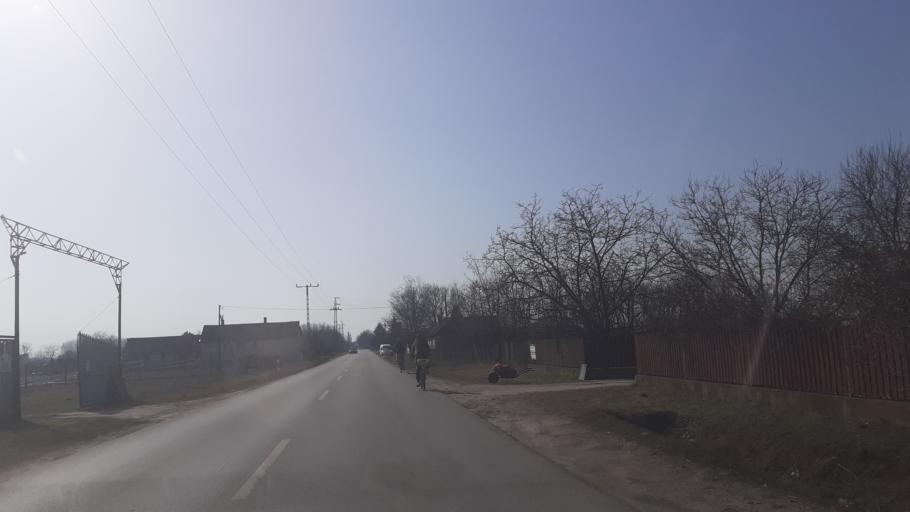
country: HU
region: Bacs-Kiskun
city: Lajosmizse
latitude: 47.0255
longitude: 19.5311
